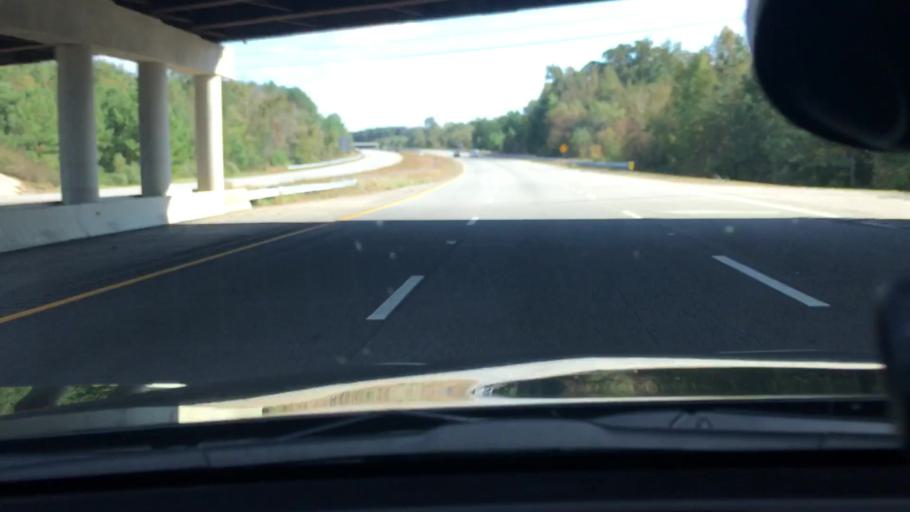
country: US
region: North Carolina
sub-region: Wilson County
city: Lucama
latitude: 35.7109
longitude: -78.0001
